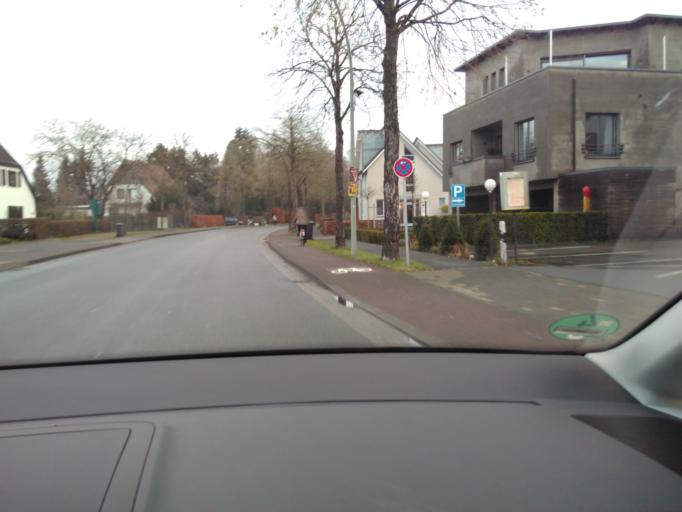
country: DE
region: North Rhine-Westphalia
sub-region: Regierungsbezirk Detmold
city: Rheda-Wiedenbruck
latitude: 51.8389
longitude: 8.3146
